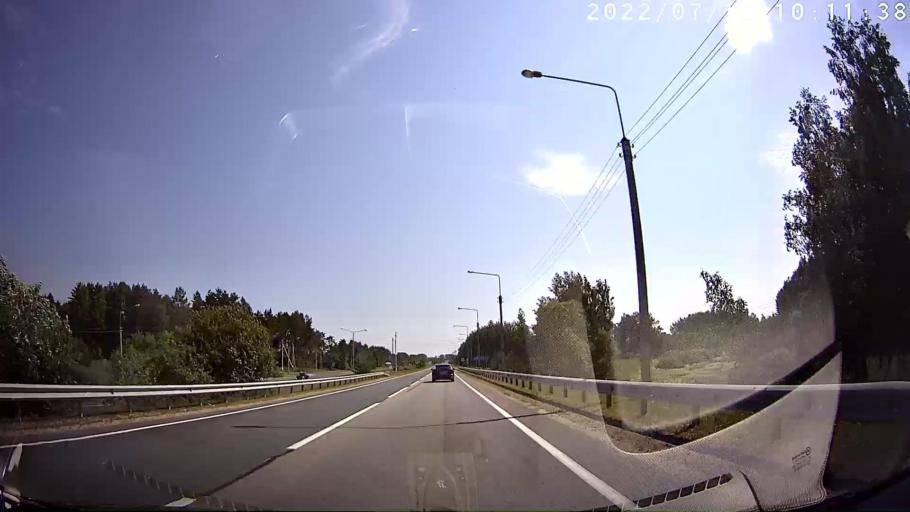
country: RU
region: Mariy-El
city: Sovetskiy
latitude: 56.7435
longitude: 48.2093
